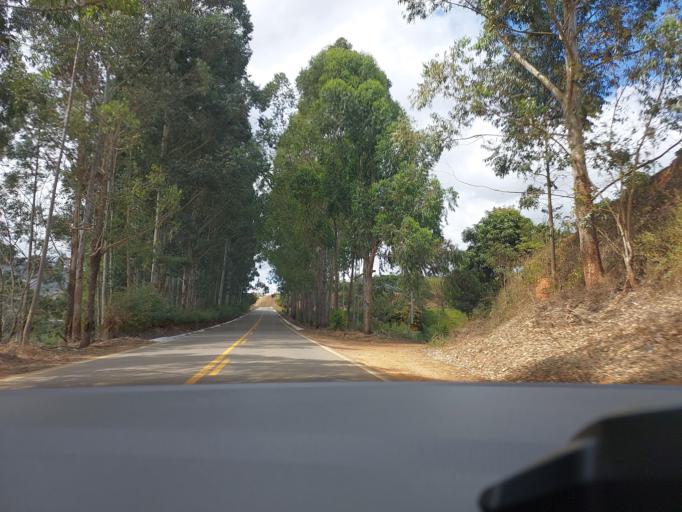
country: BR
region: Minas Gerais
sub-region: Visconde Do Rio Branco
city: Visconde do Rio Branco
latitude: -20.9465
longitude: -42.6233
